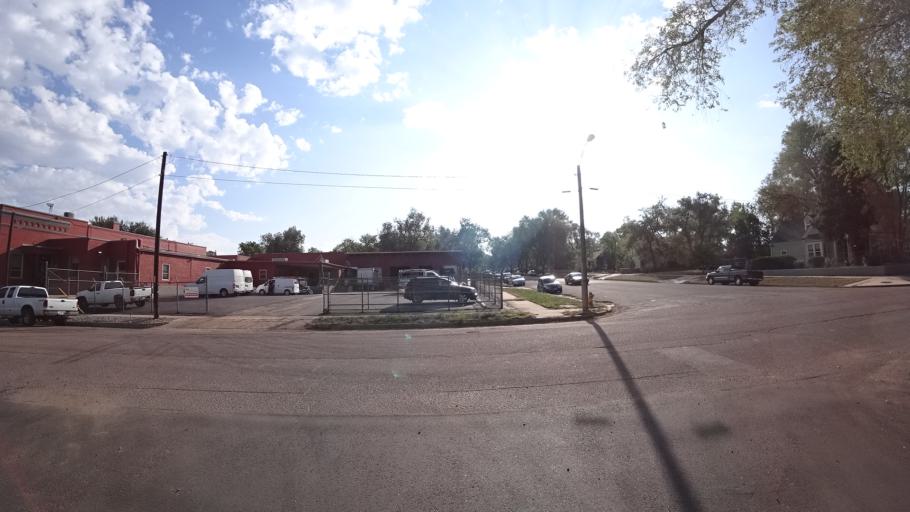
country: US
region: Colorado
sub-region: El Paso County
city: Colorado Springs
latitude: 38.8267
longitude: -104.8134
